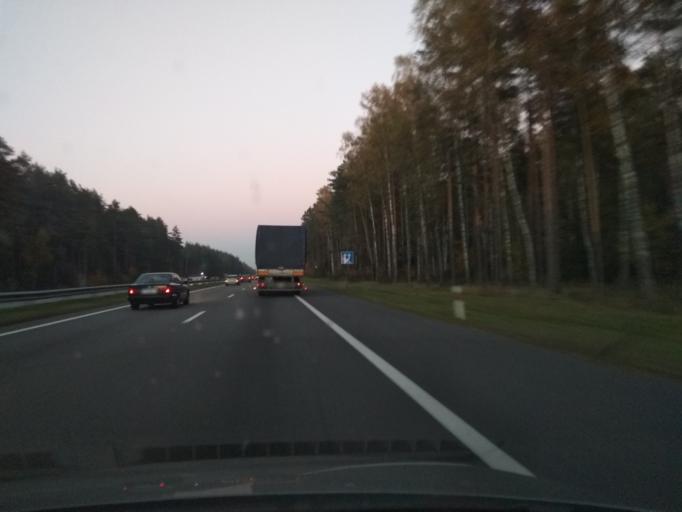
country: BY
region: Minsk
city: Enyerhyetykaw
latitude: 53.5546
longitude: 26.9681
